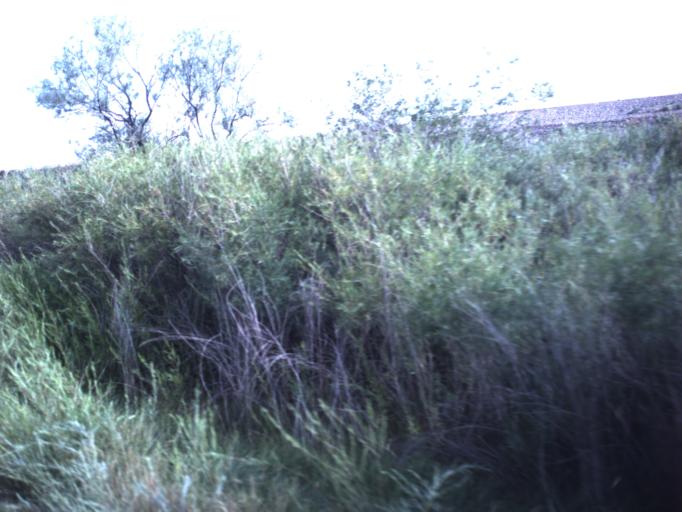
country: US
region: Utah
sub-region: Duchesne County
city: Duchesne
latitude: 40.2909
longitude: -110.2308
